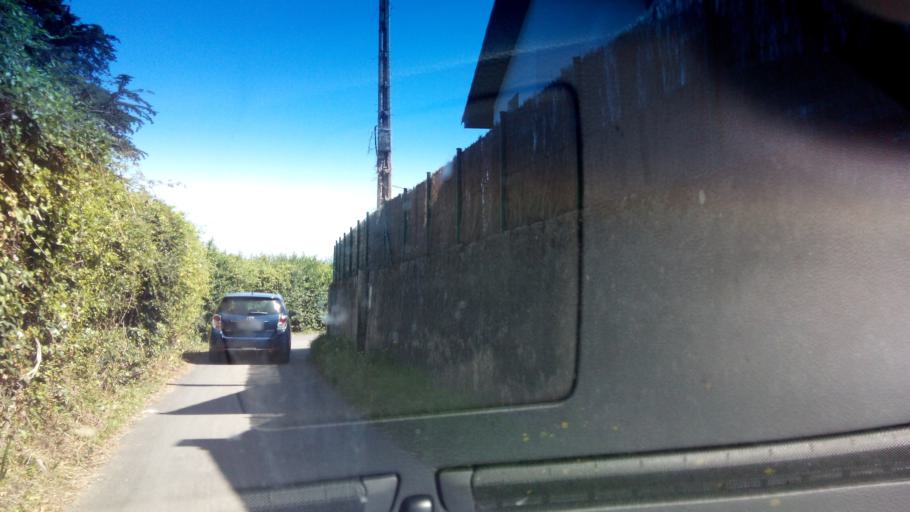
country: ES
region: Asturias
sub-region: Province of Asturias
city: Colunga
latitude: 43.4758
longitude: -5.2217
